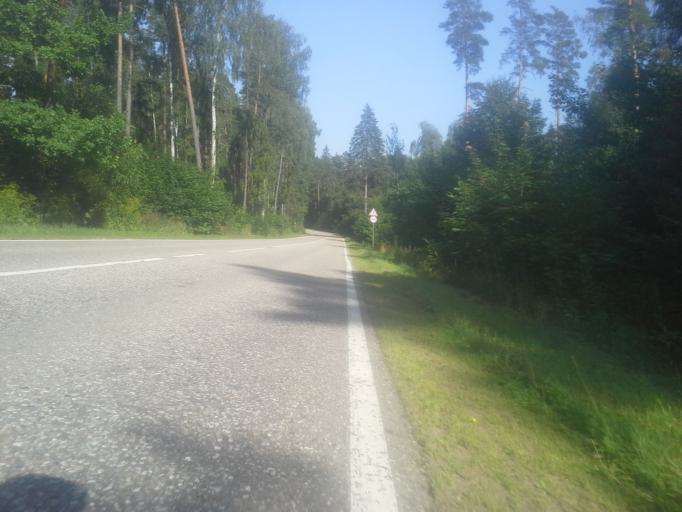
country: RU
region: Moskovskaya
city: Karinskoye
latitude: 55.6963
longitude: 36.7285
